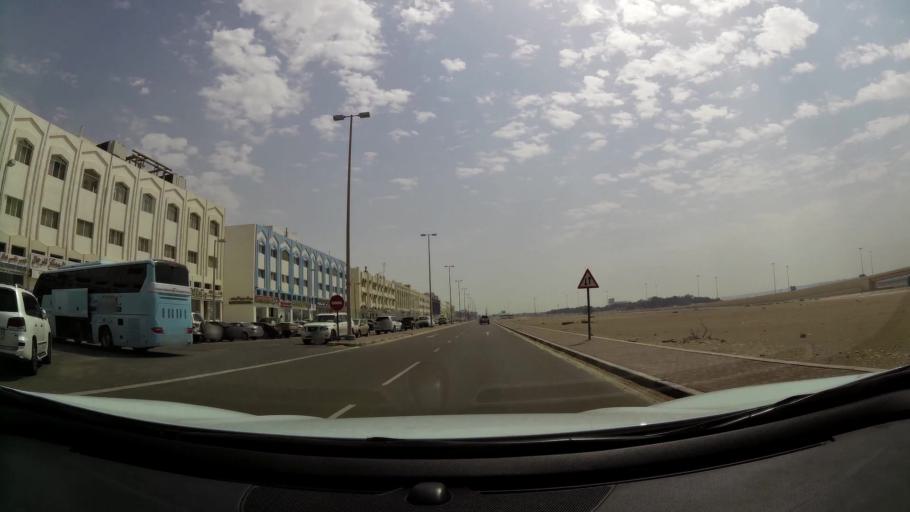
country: AE
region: Abu Dhabi
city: Abu Dhabi
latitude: 24.3107
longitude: 54.6053
